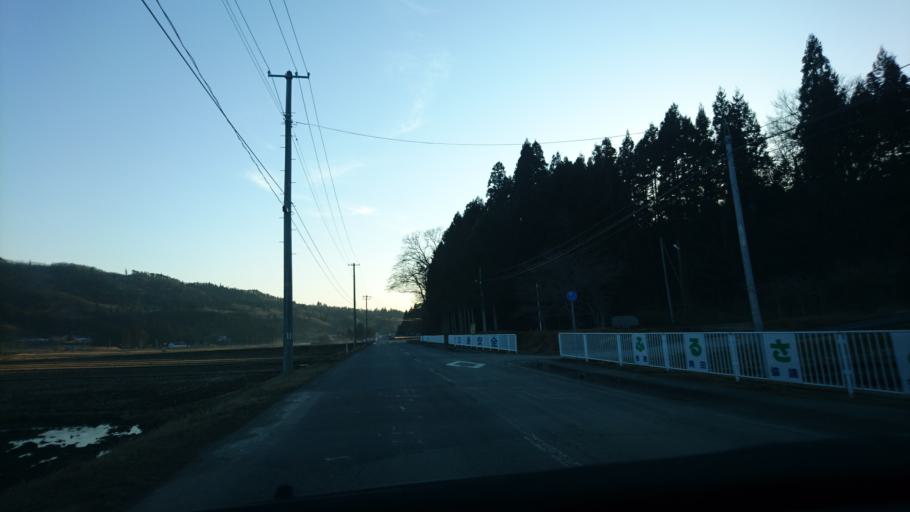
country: JP
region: Iwate
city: Mizusawa
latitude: 39.0474
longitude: 141.3611
